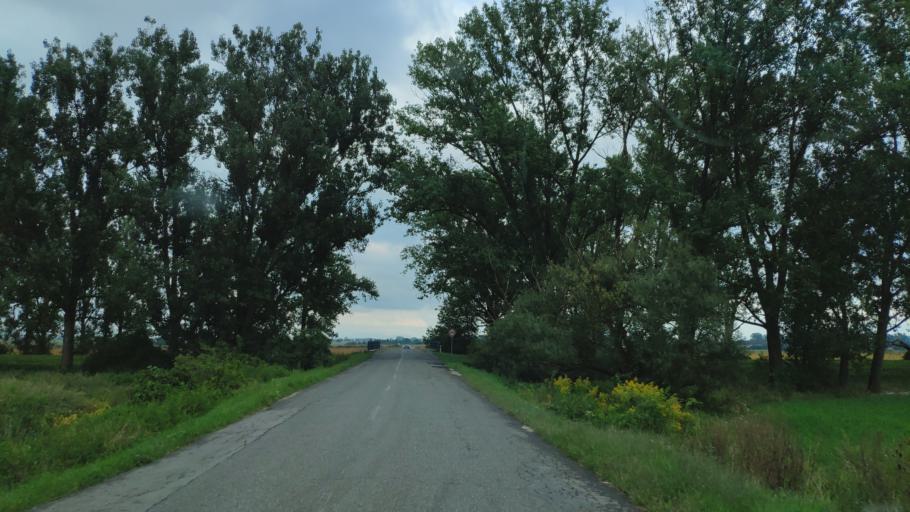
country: SK
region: Kosicky
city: Moldava nad Bodvou
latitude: 48.5822
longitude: 20.9344
